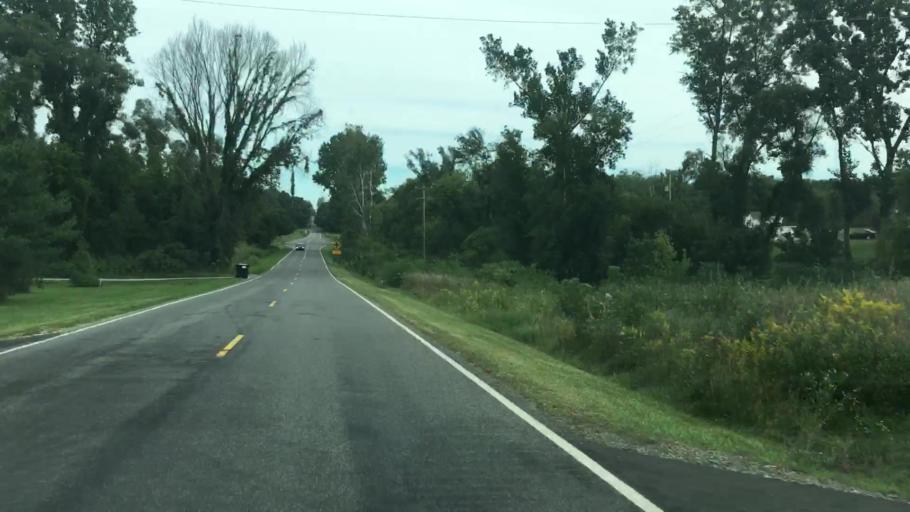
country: US
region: Michigan
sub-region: Kent County
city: Byron Center
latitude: 42.8239
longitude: -85.7828
